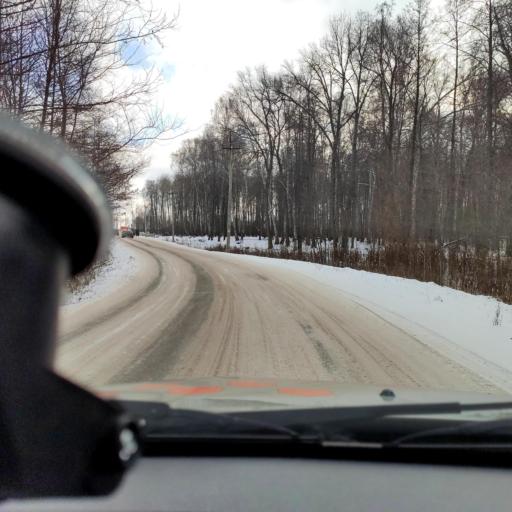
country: RU
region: Bashkortostan
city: Avdon
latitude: 54.7810
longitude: 55.7502
